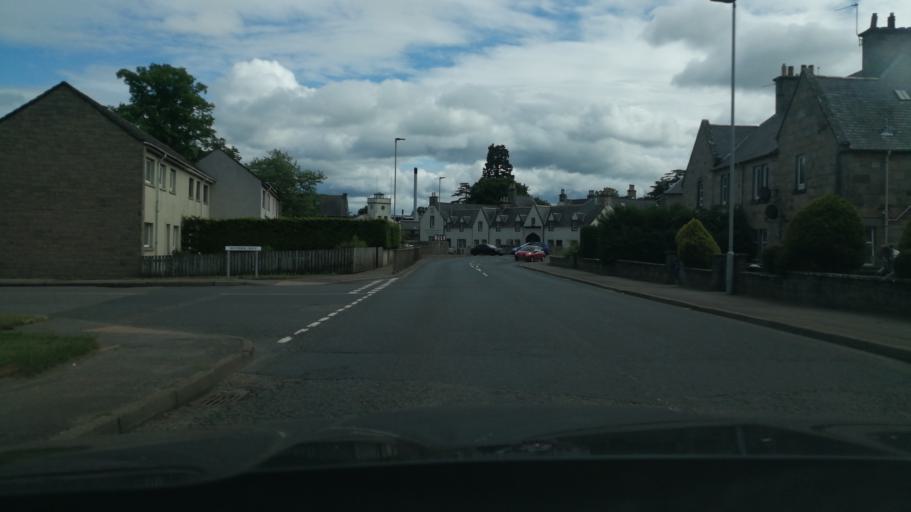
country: GB
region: Scotland
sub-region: Moray
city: Elgin
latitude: 57.6527
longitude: -3.3004
